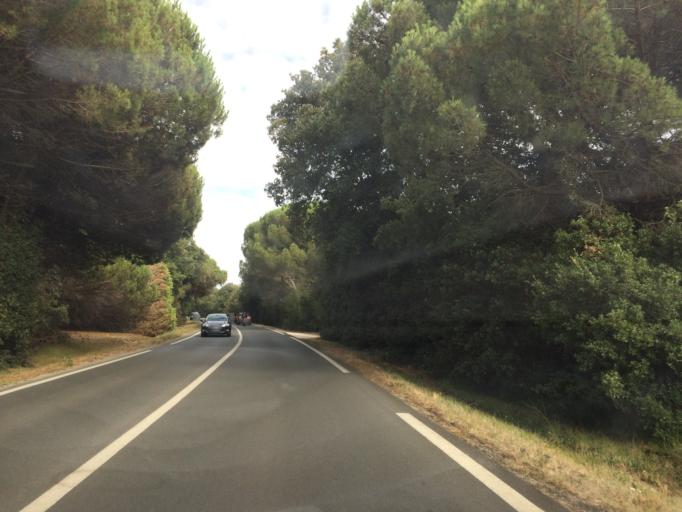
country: FR
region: Poitou-Charentes
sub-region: Departement de la Charente-Maritime
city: La Flotte
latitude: 46.1790
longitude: -1.3320
